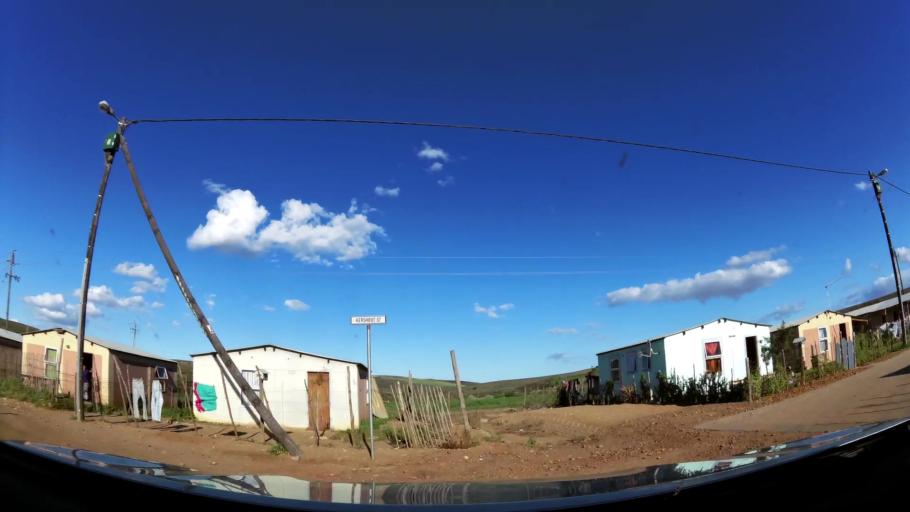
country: ZA
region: Western Cape
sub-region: Eden District Municipality
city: Riversdale
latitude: -34.1092
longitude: 20.9661
